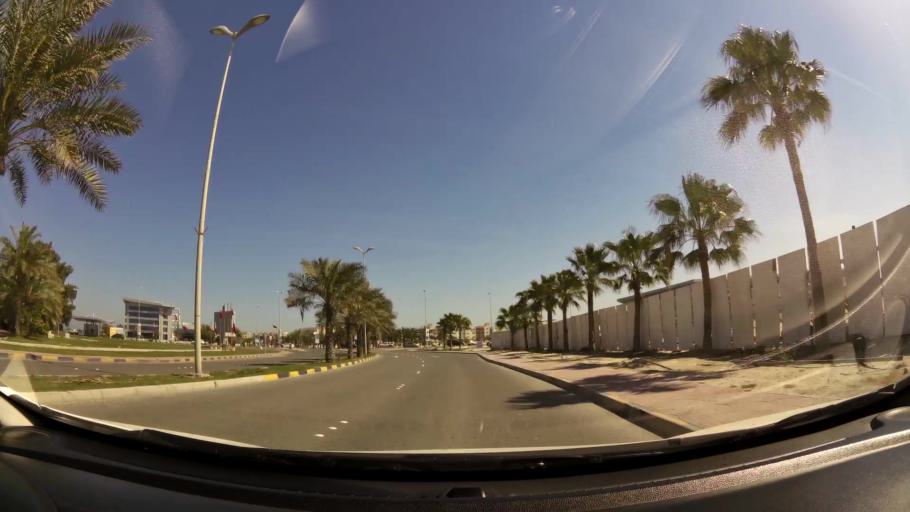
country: BH
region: Muharraq
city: Al Hadd
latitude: 26.2787
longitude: 50.6620
